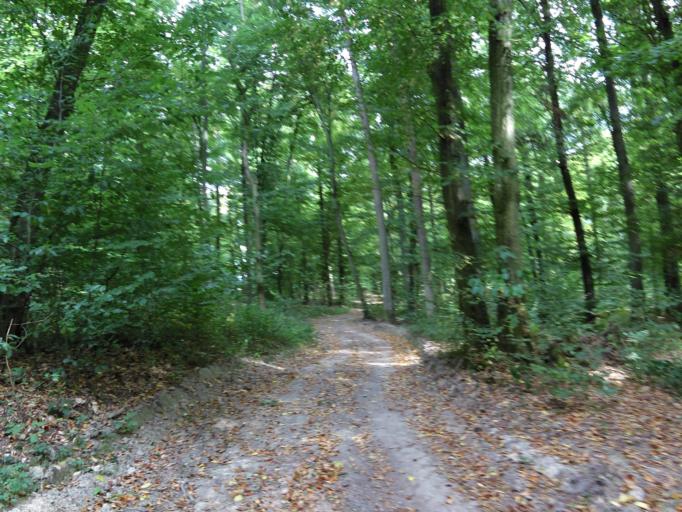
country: DE
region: Bavaria
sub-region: Regierungsbezirk Unterfranken
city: Hochberg
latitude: 49.7865
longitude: 9.8683
